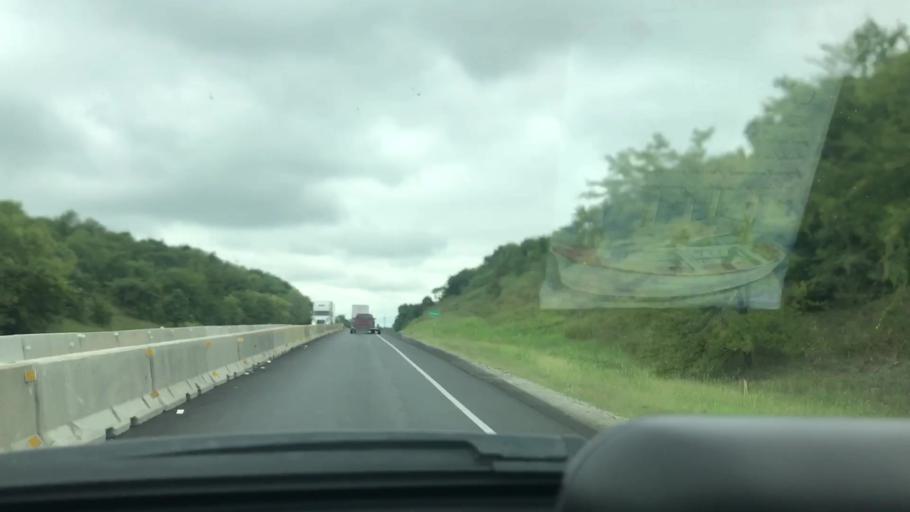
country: US
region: Oklahoma
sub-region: McIntosh County
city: Eufaula
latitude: 35.2700
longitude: -95.5918
